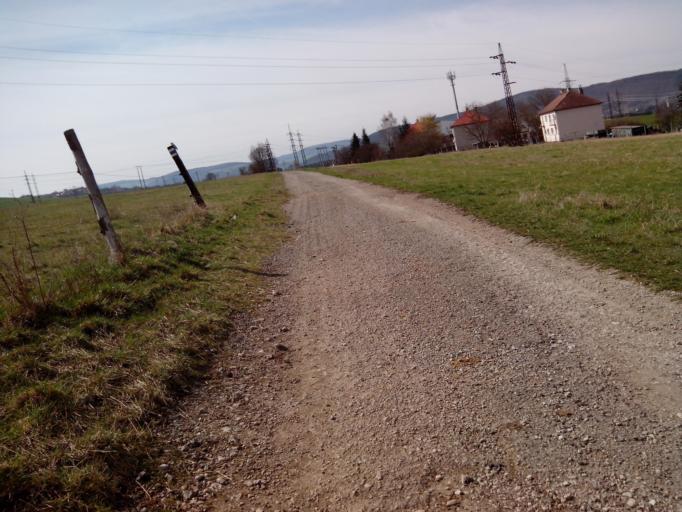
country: CZ
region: Central Bohemia
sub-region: Okres Beroun
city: Beroun
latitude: 49.9525
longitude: 14.0890
